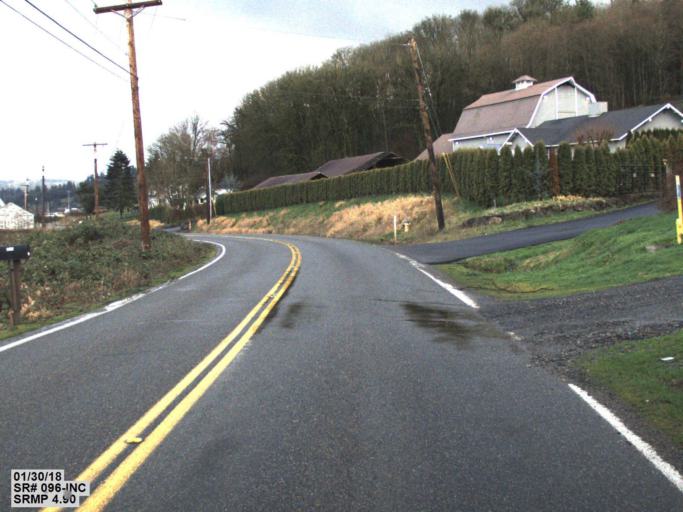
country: US
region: Washington
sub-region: Snohomish County
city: Silver Firs
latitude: 47.8902
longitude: -122.1431
